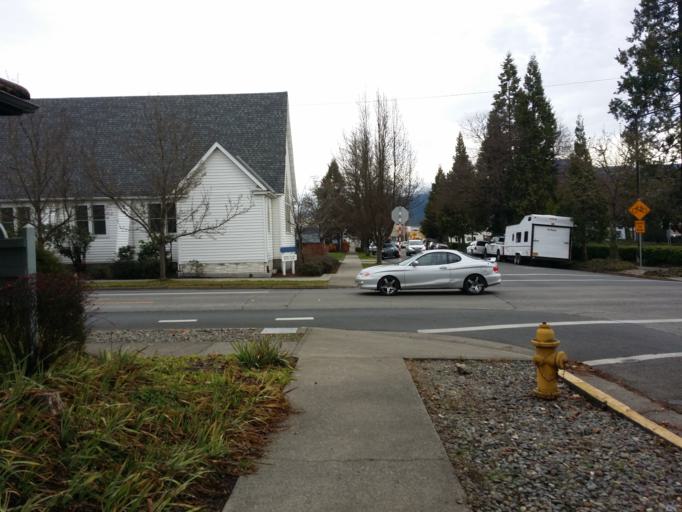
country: US
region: Oregon
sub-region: Josephine County
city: Grants Pass
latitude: 42.4424
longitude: -123.3283
